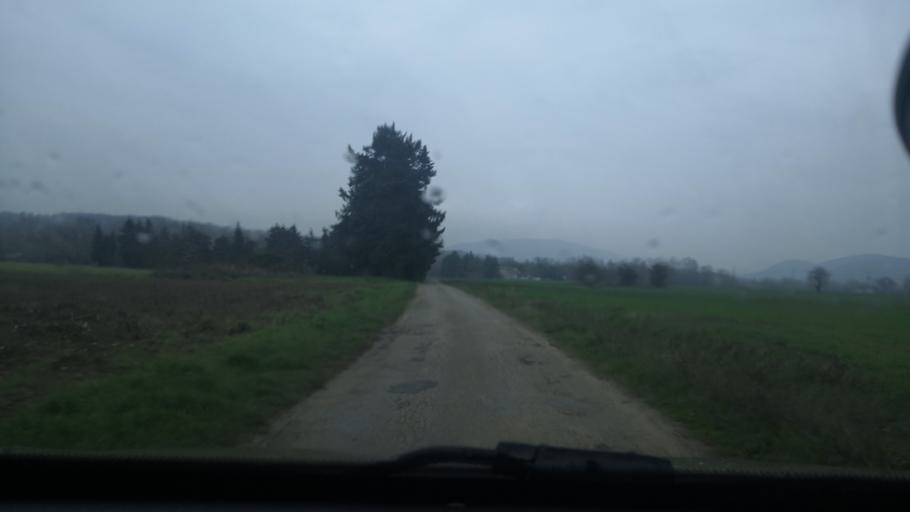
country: FR
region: Rhone-Alpes
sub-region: Departement de la Drome
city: Saint-Marcel-les-Sauzet
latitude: 44.5776
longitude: 4.8107
